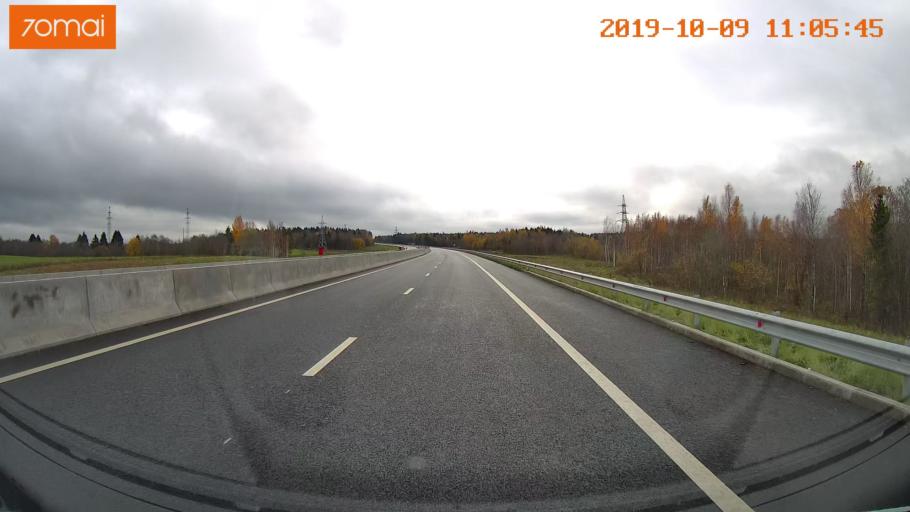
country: RU
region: Vologda
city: Molochnoye
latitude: 59.1956
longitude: 39.7580
